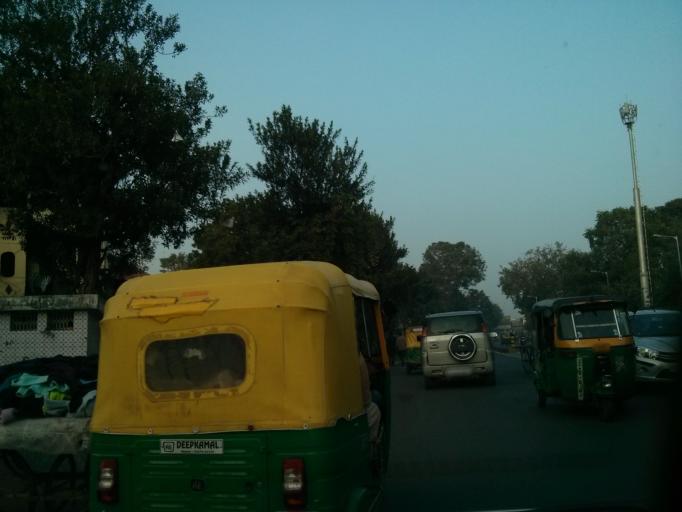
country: IN
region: Gujarat
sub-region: Ahmadabad
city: Ahmedabad
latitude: 23.0339
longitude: 72.5853
